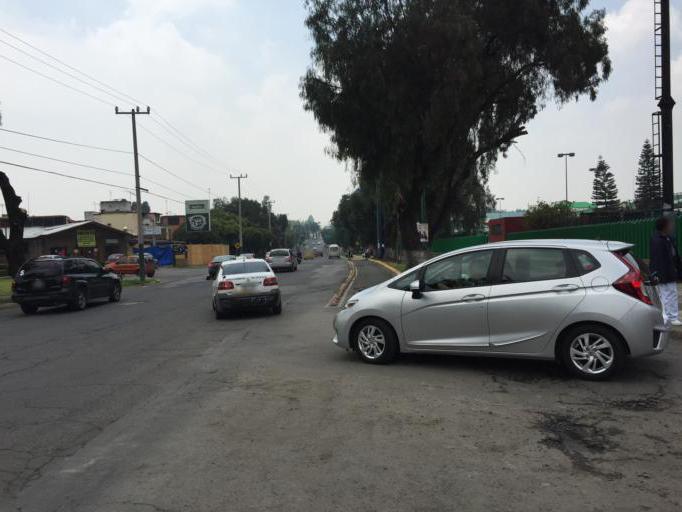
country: MX
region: Mexico
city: Cuautitlan Izcalli
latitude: 19.6482
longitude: -99.2048
